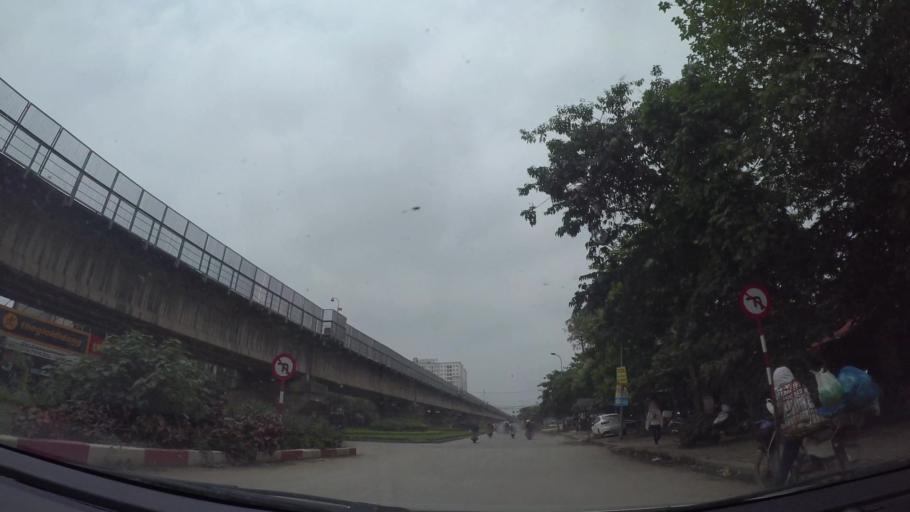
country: VN
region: Ha Noi
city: Tay Ho
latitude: 21.0800
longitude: 105.7857
